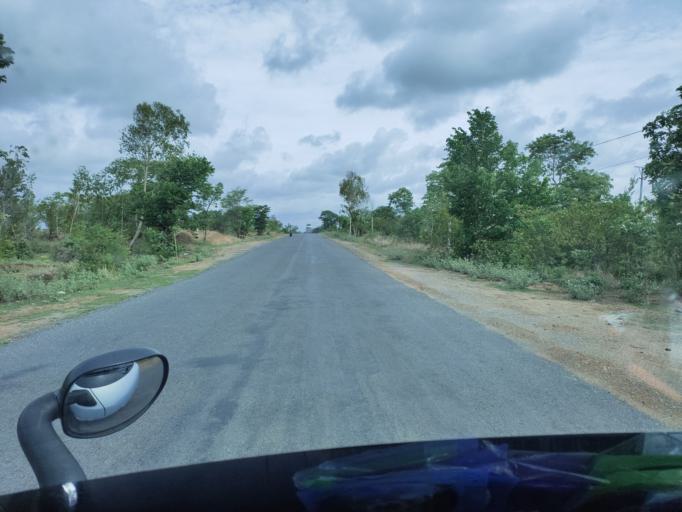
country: MM
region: Magway
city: Chauk
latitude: 20.9747
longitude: 95.0530
